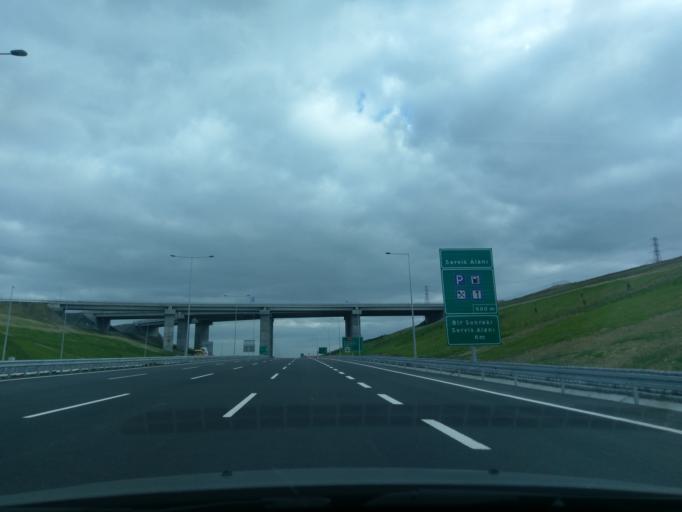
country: TR
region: Istanbul
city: Durusu
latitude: 41.2449
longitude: 28.6920
